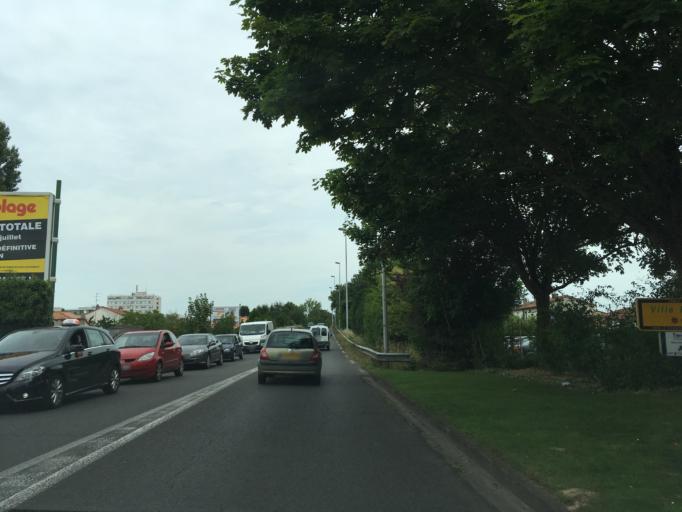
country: FR
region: Poitou-Charentes
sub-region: Departement des Deux-Sevres
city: Niort
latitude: 46.3136
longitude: -0.4652
